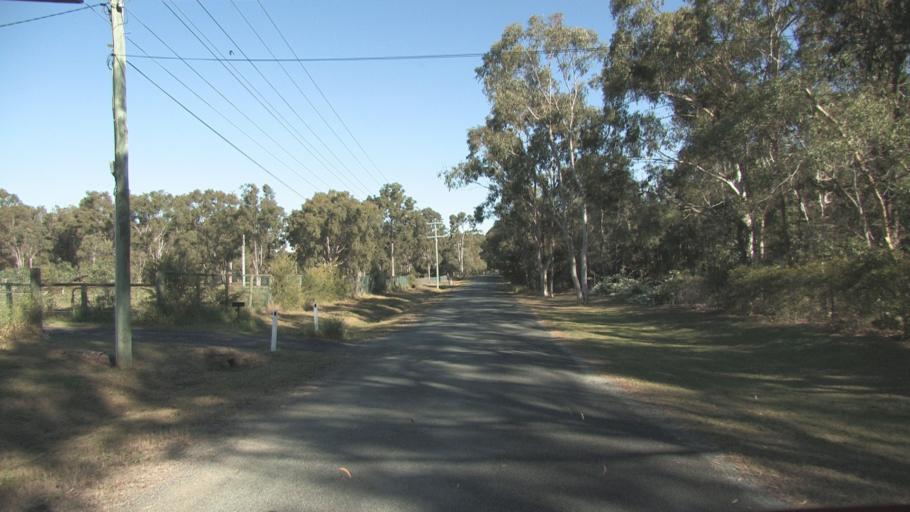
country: AU
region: Queensland
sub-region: Logan
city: Logan Reserve
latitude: -27.7298
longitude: 153.0833
